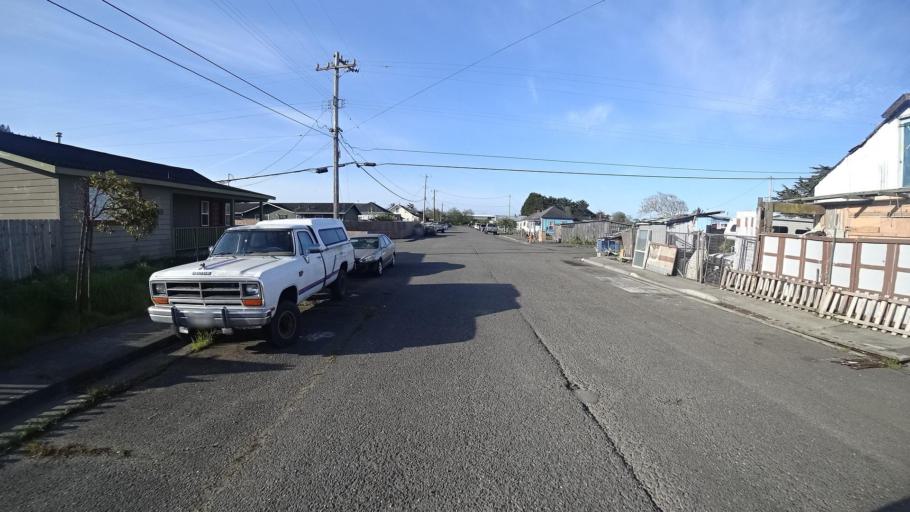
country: US
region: California
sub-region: Humboldt County
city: Humboldt Hill
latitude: 40.7246
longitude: -124.2177
